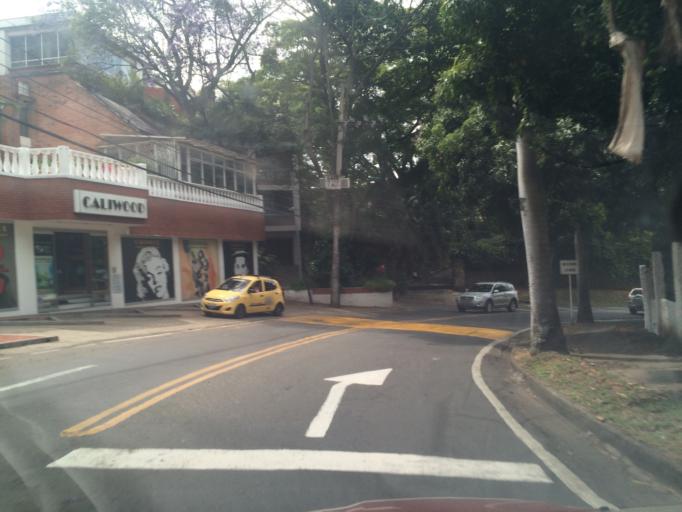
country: CO
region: Valle del Cauca
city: Cali
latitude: 3.4503
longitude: -76.5470
